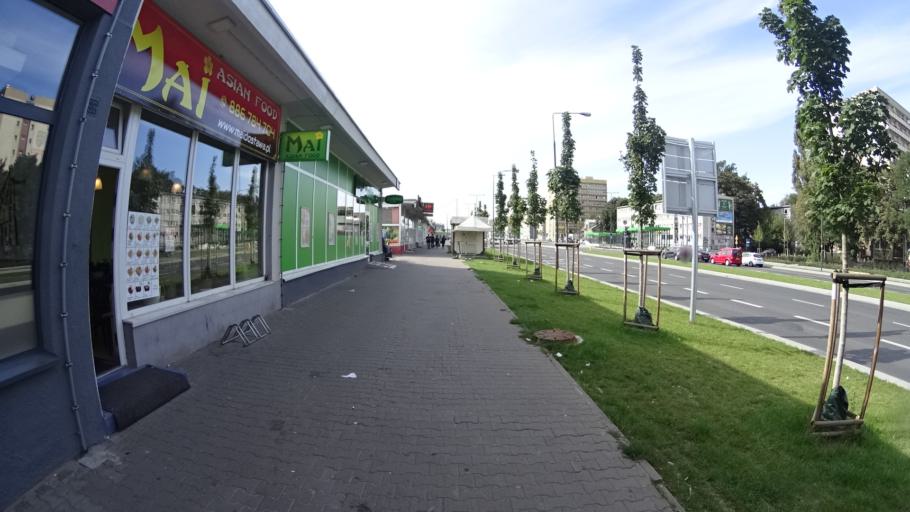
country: PL
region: Masovian Voivodeship
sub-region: Warszawa
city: Bemowo
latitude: 52.2386
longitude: 20.9467
